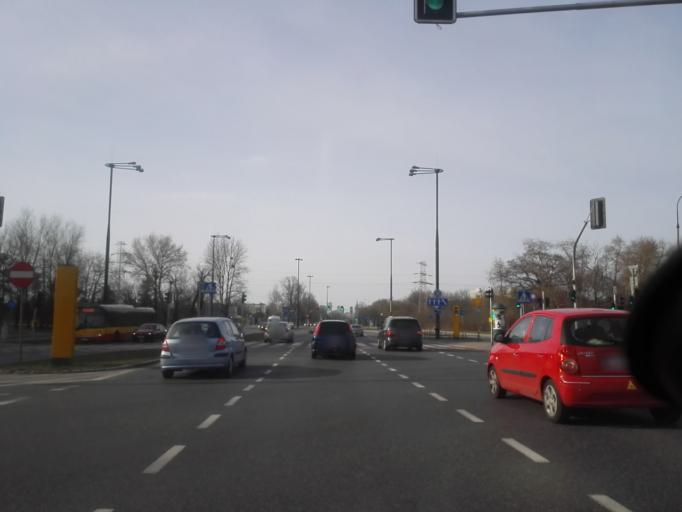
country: PL
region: Masovian Voivodeship
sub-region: Warszawa
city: Mokotow
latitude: 52.1905
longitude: 21.0468
